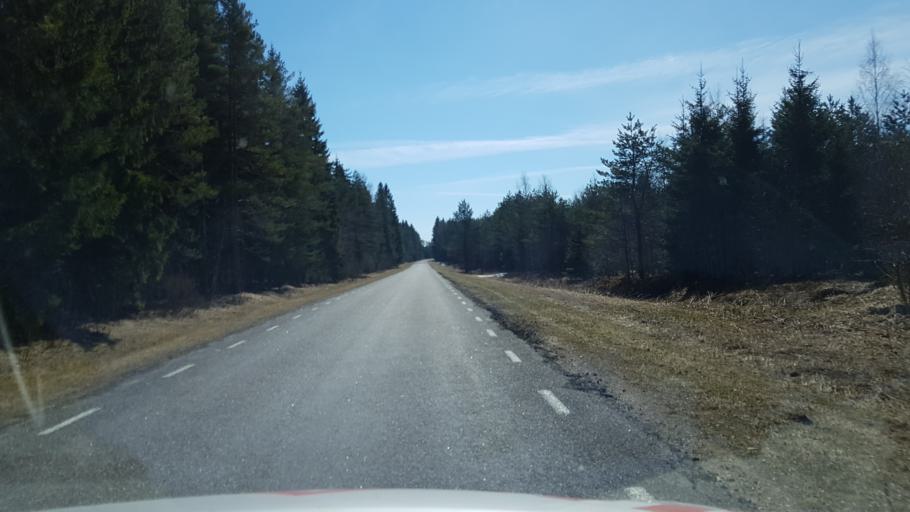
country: EE
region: Laeaene-Virumaa
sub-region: Vinni vald
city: Vinni
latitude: 59.1446
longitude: 26.5222
